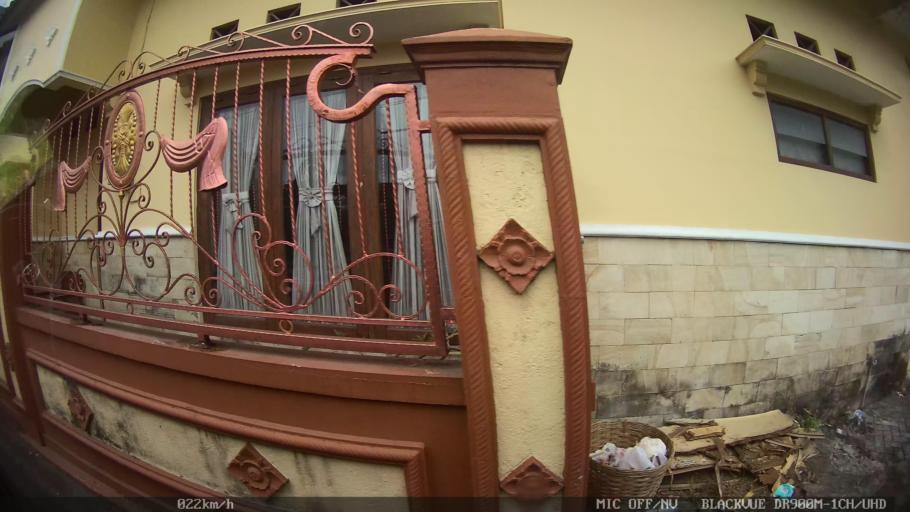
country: ID
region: Daerah Istimewa Yogyakarta
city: Depok
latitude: -7.8112
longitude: 110.4111
